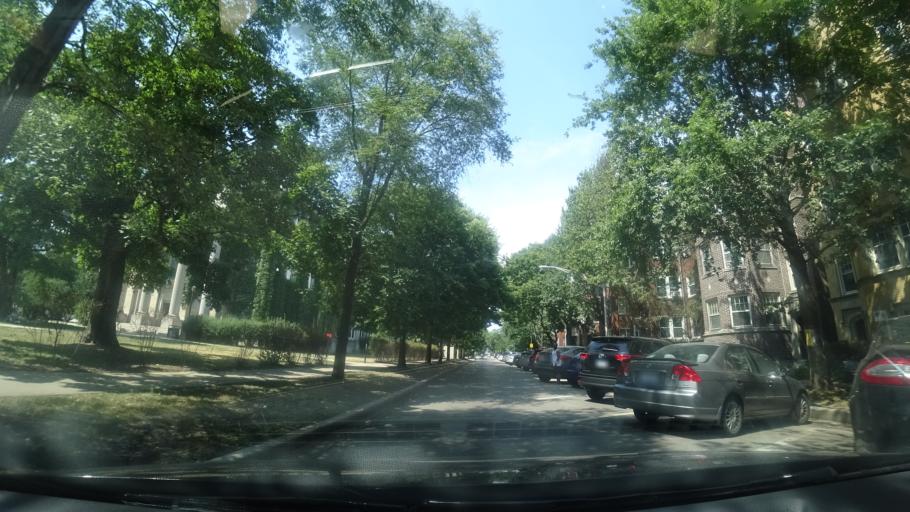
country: US
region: Illinois
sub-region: Cook County
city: Evanston
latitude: 41.9899
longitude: -87.6651
